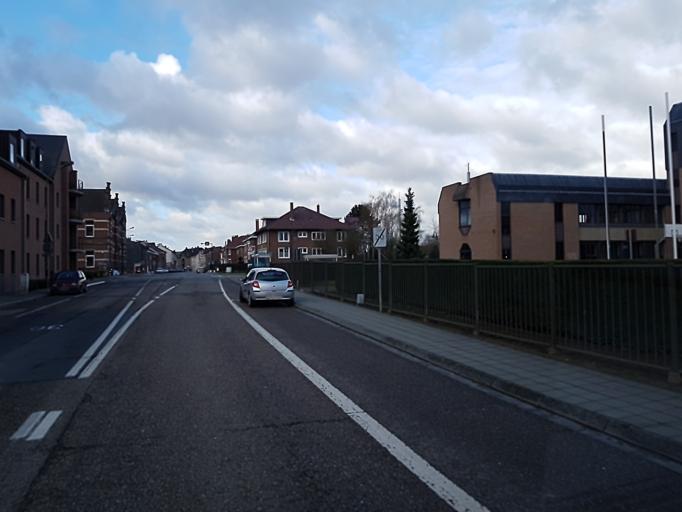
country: BE
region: Wallonia
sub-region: Province du Brabant Wallon
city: Jodoigne
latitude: 50.7278
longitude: 4.8754
